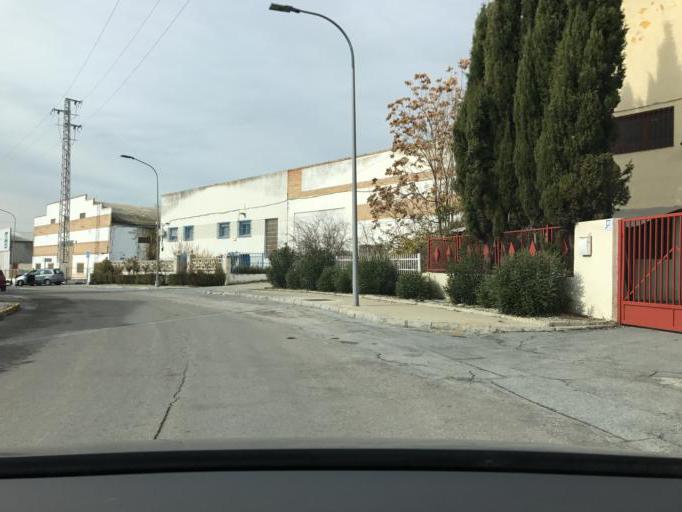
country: ES
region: Andalusia
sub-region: Provincia de Granada
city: Peligros
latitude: 37.2278
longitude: -3.6250
